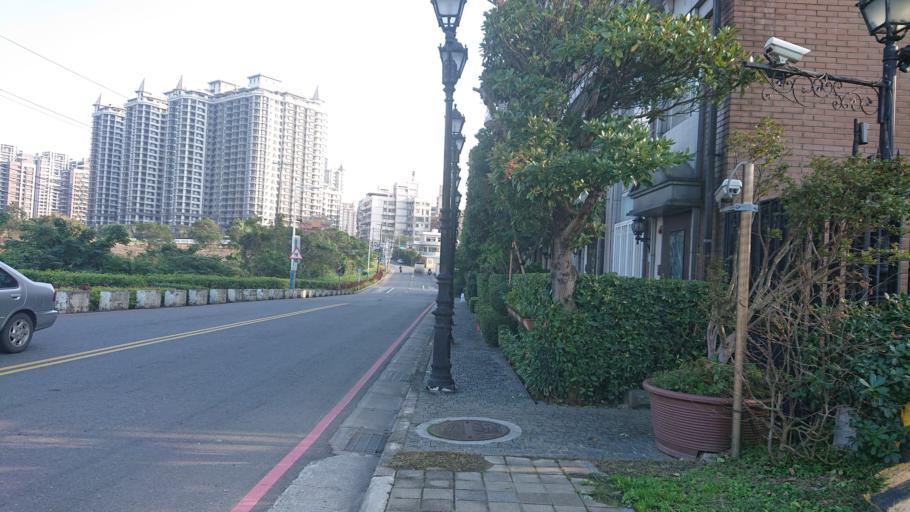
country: TW
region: Taipei
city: Taipei
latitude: 25.1910
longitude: 121.4258
